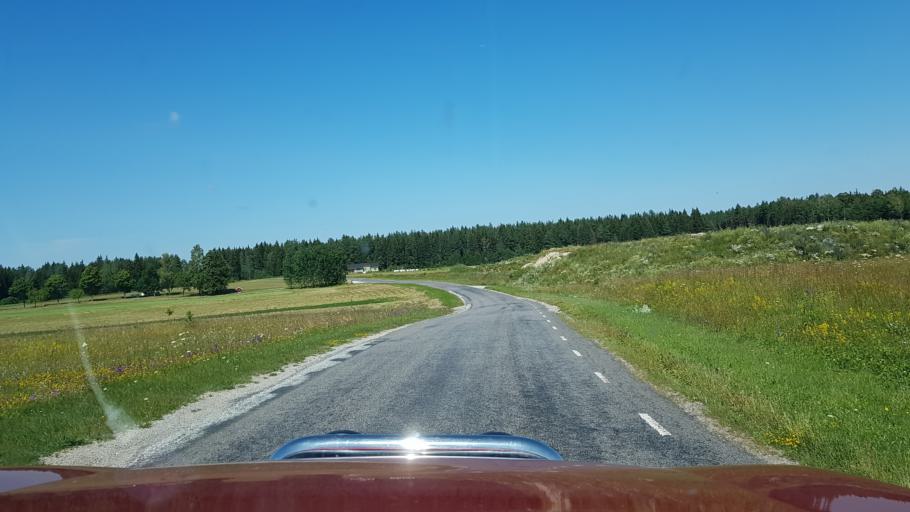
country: EE
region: Harju
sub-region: Saue linn
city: Saue
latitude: 59.1667
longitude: 24.5007
